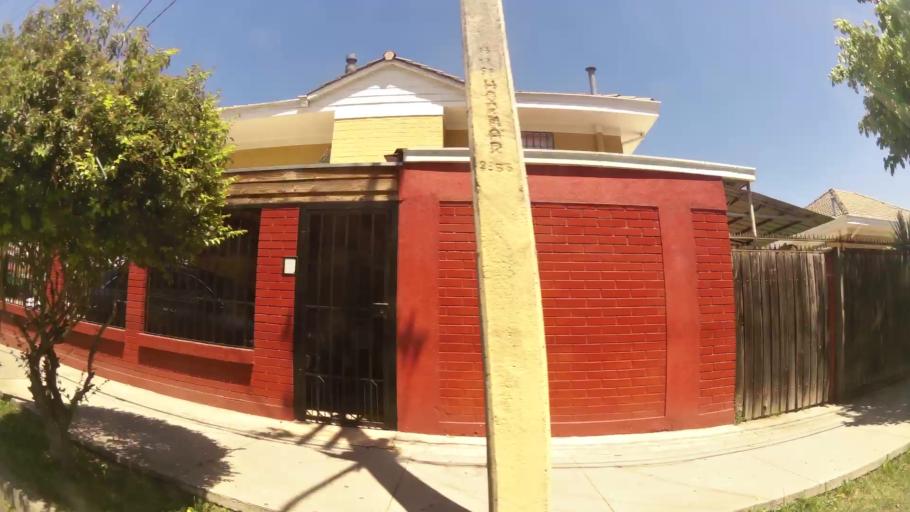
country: CL
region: Santiago Metropolitan
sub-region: Provincia de Maipo
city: San Bernardo
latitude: -33.6226
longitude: -70.7132
